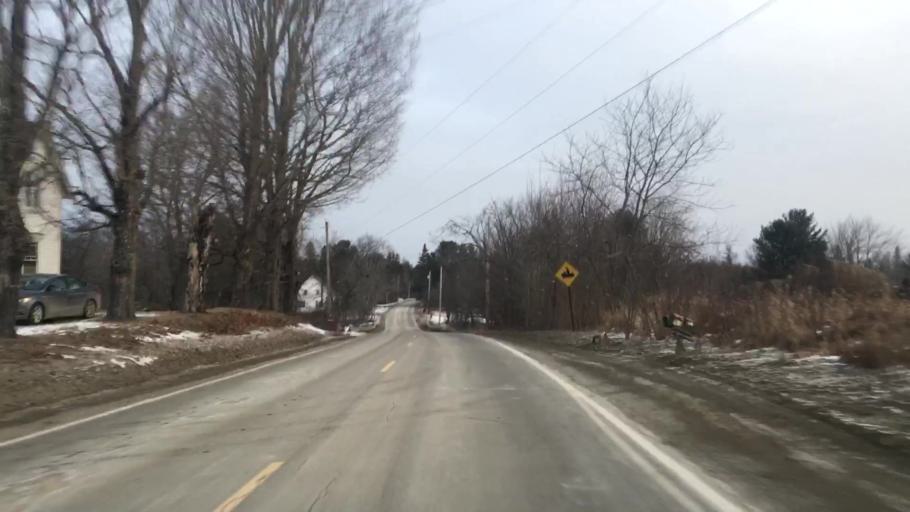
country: US
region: Maine
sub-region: Hancock County
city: Franklin
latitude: 44.6865
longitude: -68.3499
